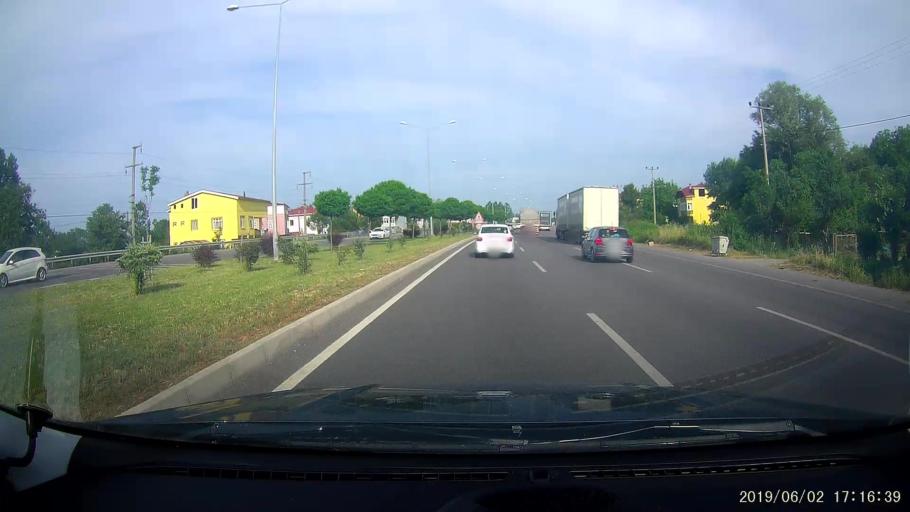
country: TR
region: Samsun
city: Dikbiyik
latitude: 41.2335
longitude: 36.5697
